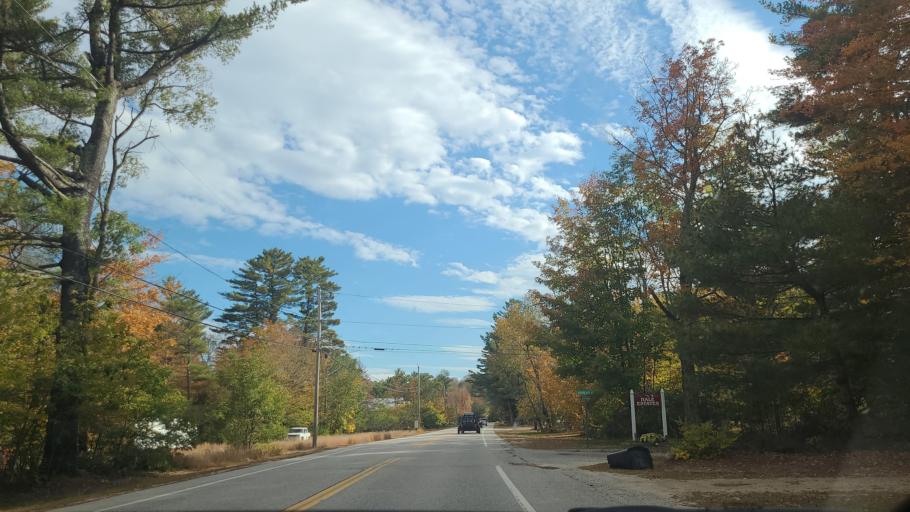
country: US
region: New Hampshire
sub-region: Carroll County
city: Conway
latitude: 44.0051
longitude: -71.1303
